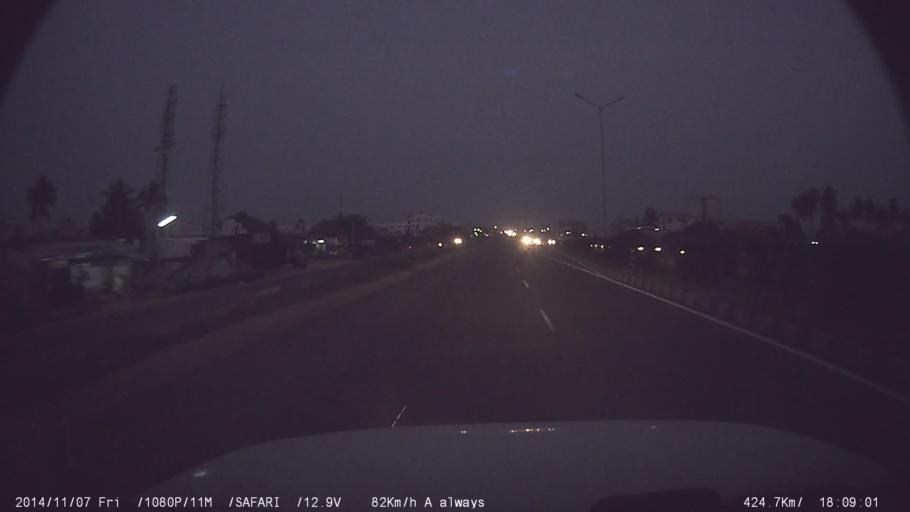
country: IN
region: Tamil Nadu
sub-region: Erode
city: Bhavani
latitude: 11.4323
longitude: 77.6930
